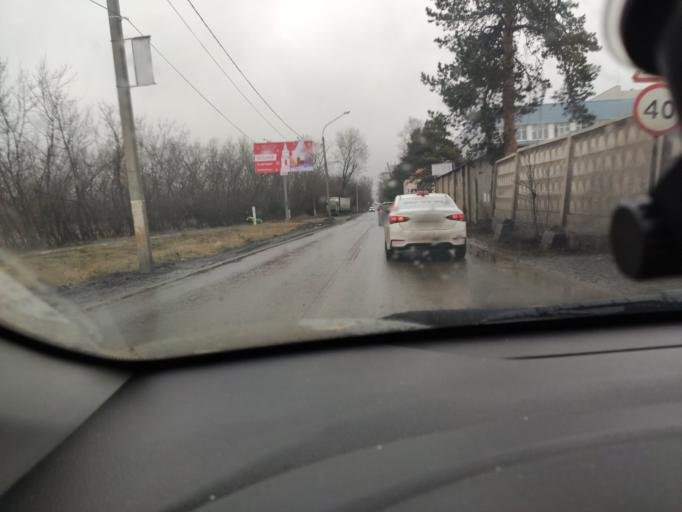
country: RU
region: Moskovskaya
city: Biryulevo Zapadnoye
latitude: 55.5646
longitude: 37.6454
